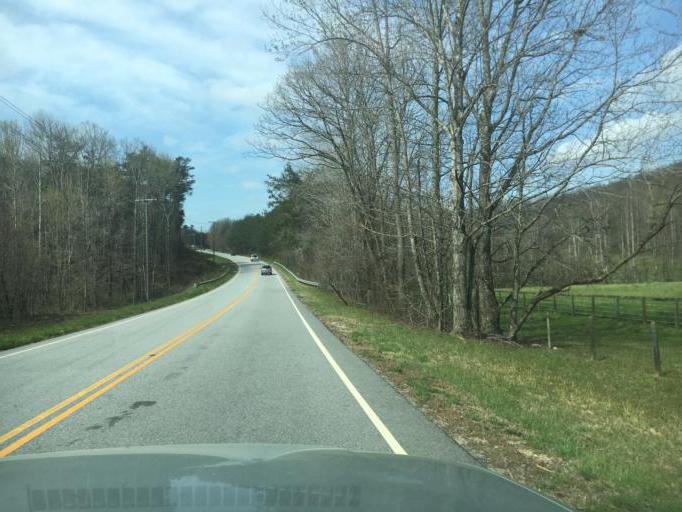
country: US
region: South Carolina
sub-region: Greenville County
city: Tigerville
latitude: 35.1250
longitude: -82.3042
